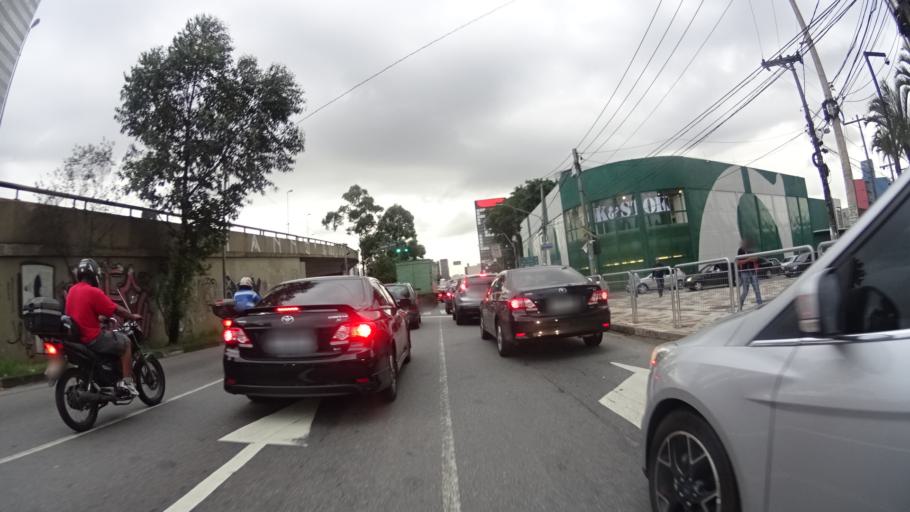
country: BR
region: Sao Paulo
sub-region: Sao Paulo
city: Sao Paulo
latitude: -23.5725
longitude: -46.7033
